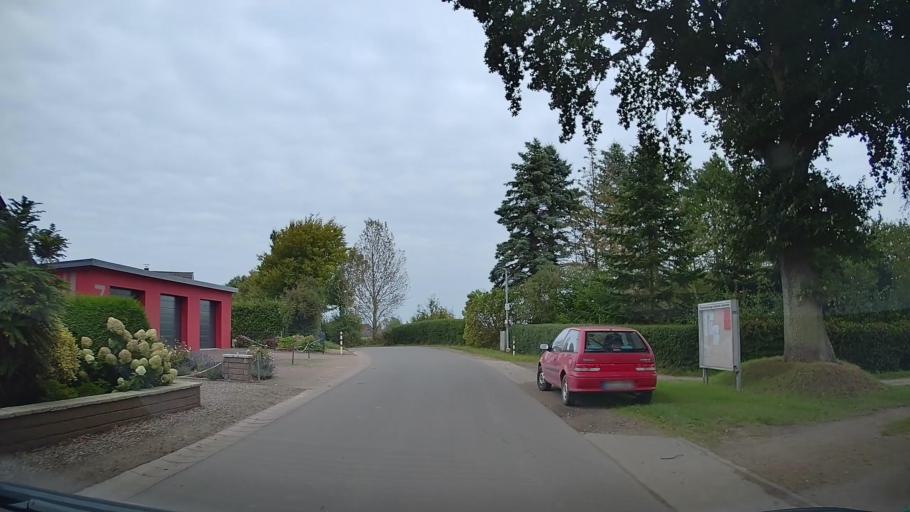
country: DE
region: Schleswig-Holstein
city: Hohenfelde
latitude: 54.3709
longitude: 10.5142
